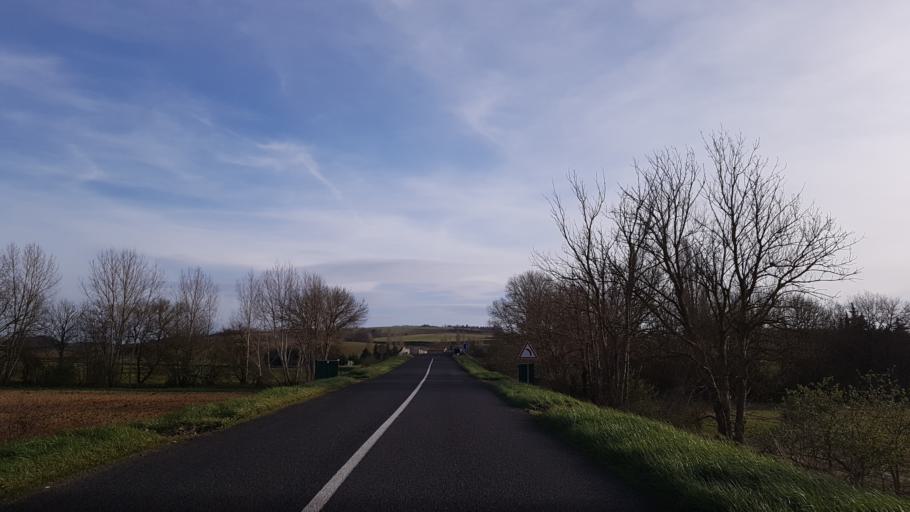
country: FR
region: Languedoc-Roussillon
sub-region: Departement de l'Aude
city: Villeneuve-la-Comptal
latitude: 43.1891
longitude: 1.9029
